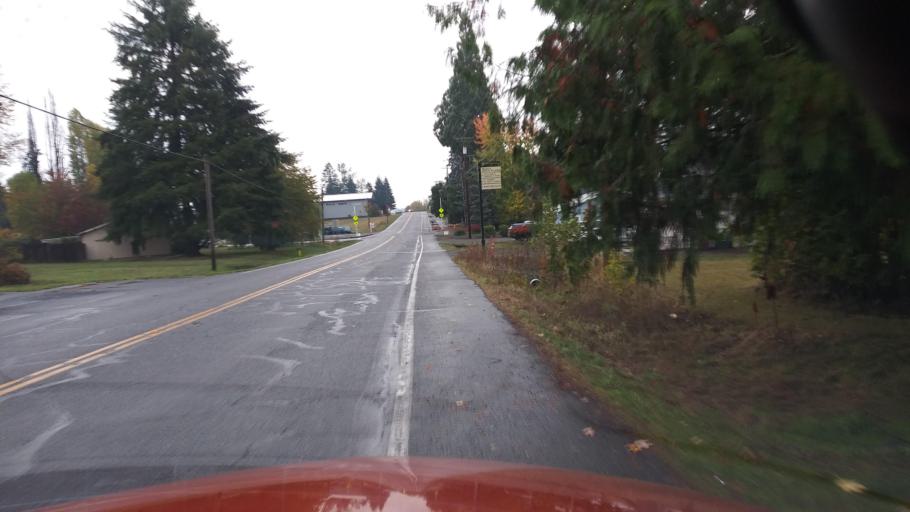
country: US
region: Oregon
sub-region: Washington County
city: North Plains
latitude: 45.5975
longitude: -122.9987
